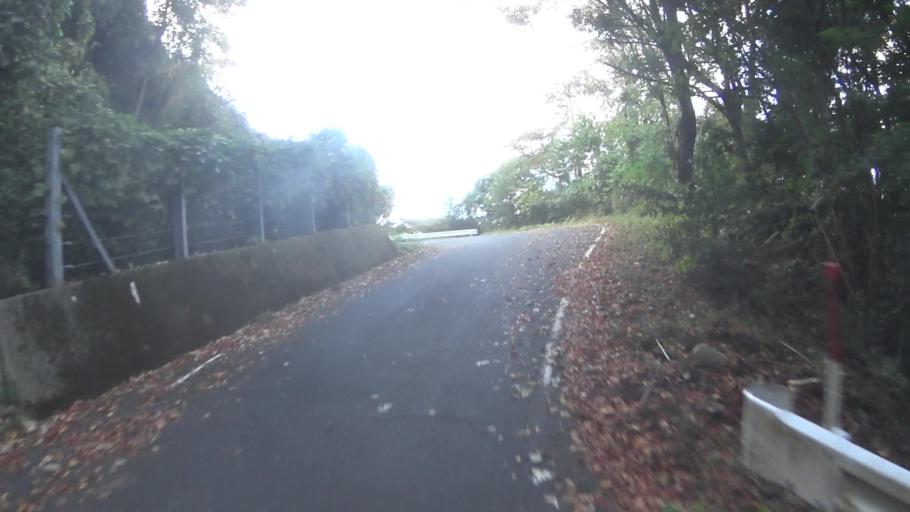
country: JP
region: Kyoto
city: Maizuru
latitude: 35.5672
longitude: 135.4192
